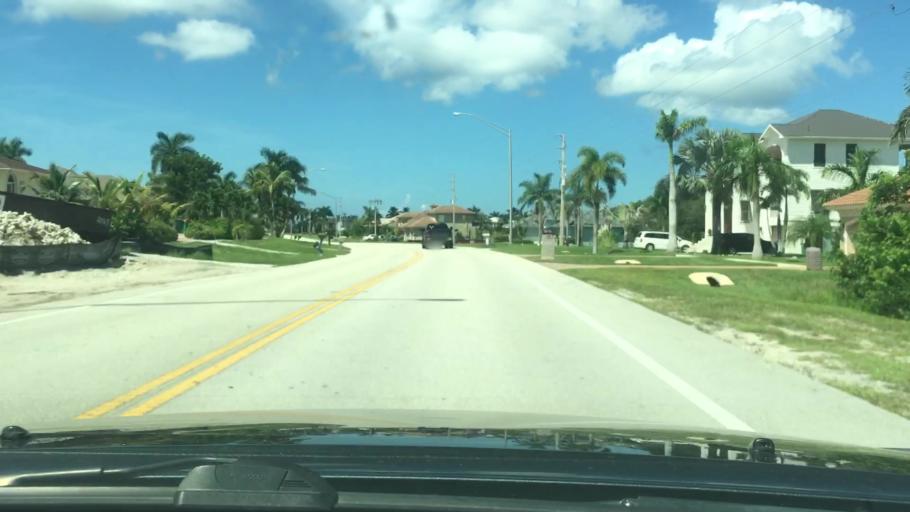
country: US
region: Florida
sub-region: Collier County
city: Marco
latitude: 25.9383
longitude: -81.6887
